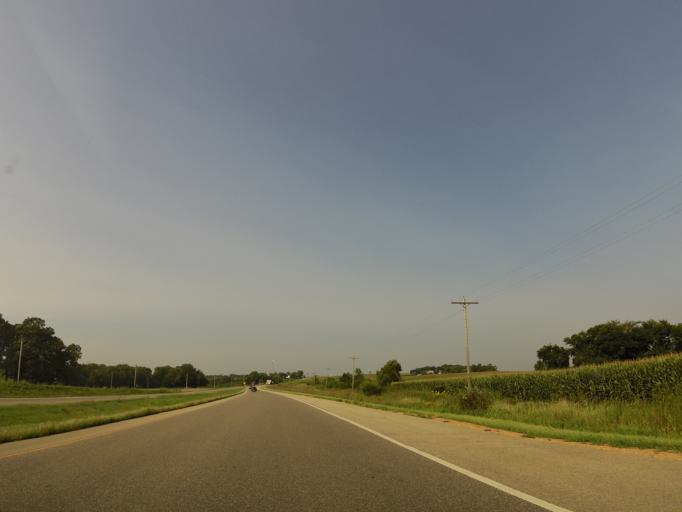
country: US
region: Minnesota
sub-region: Carver County
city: Carver
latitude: 44.7759
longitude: -93.6557
